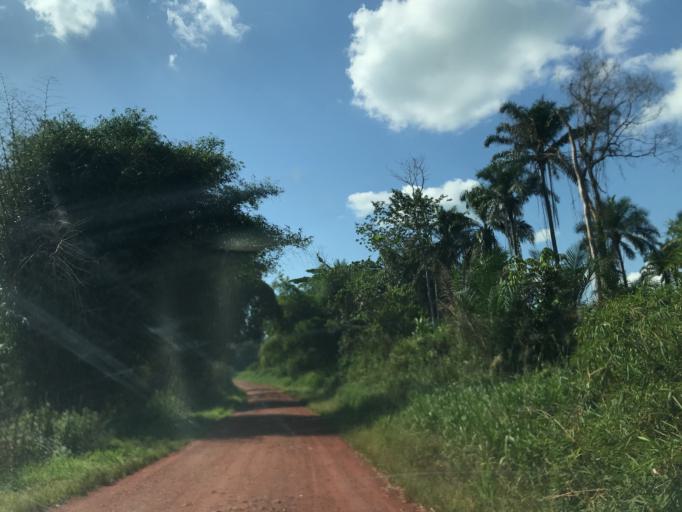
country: CD
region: Eastern Province
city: Kisangani
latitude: 1.2234
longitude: 25.2687
